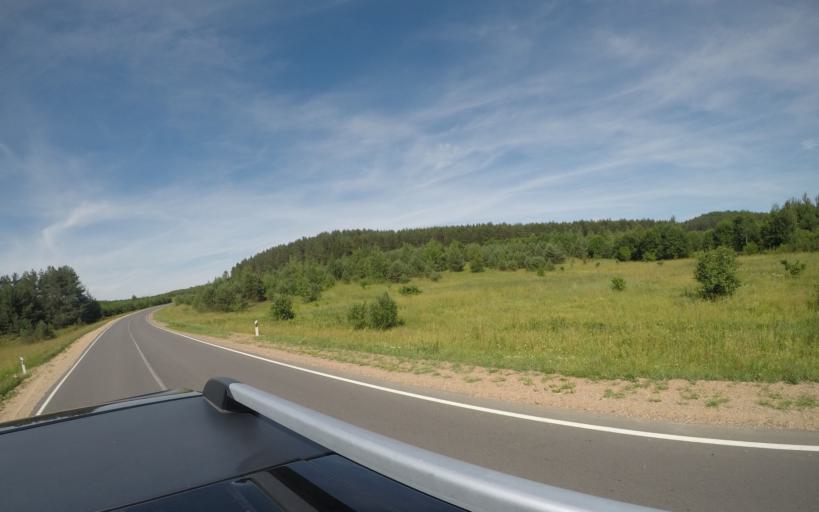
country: BY
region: Grodnenskaya
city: Hal'shany
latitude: 54.2701
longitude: 26.0314
